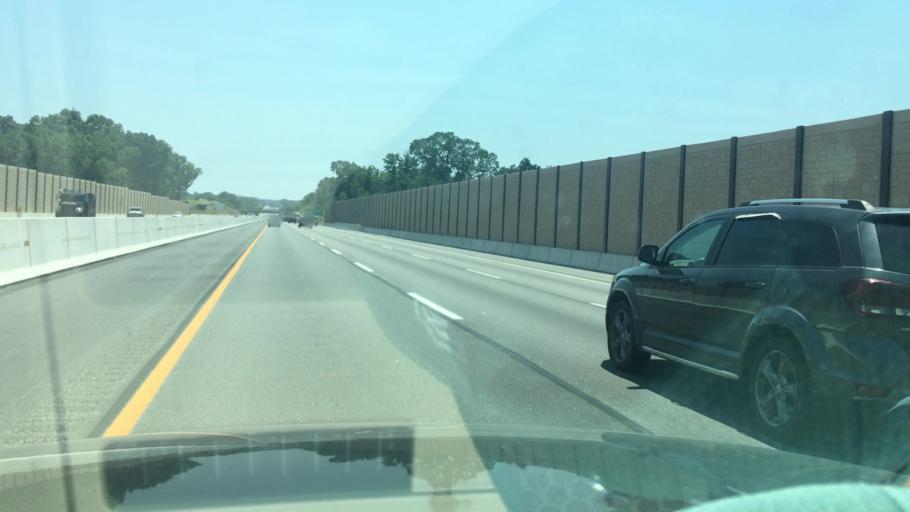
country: US
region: Pennsylvania
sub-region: Montgomery County
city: Kulpsville
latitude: 40.2353
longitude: -75.3385
